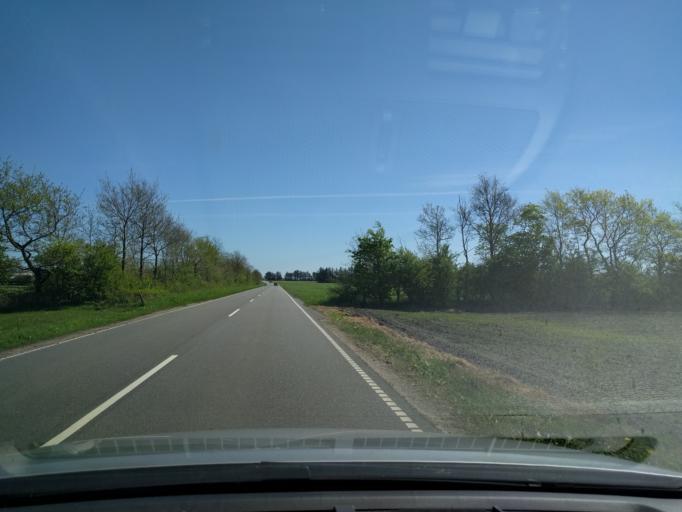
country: DK
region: South Denmark
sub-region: Billund Kommune
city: Grindsted
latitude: 55.6845
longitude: 8.8878
